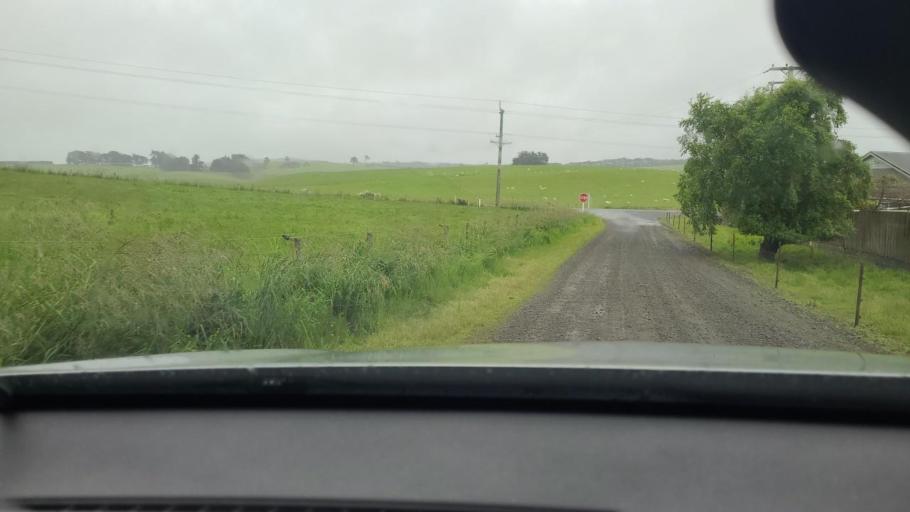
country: NZ
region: Southland
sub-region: Southland District
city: Riverton
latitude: -46.2176
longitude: 168.0532
